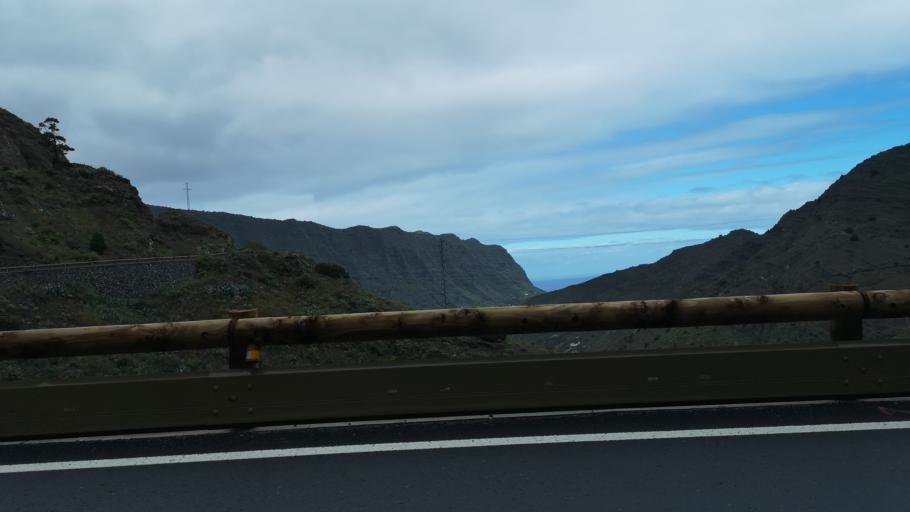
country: ES
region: Canary Islands
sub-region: Provincia de Santa Cruz de Tenerife
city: Hermigua
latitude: 28.1439
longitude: -17.1986
